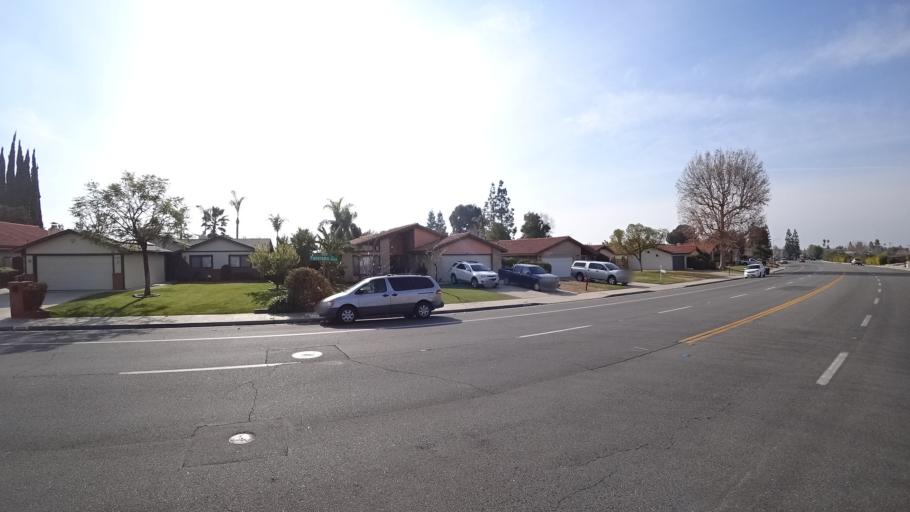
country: US
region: California
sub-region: Kern County
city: Oildale
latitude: 35.4104
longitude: -118.9426
